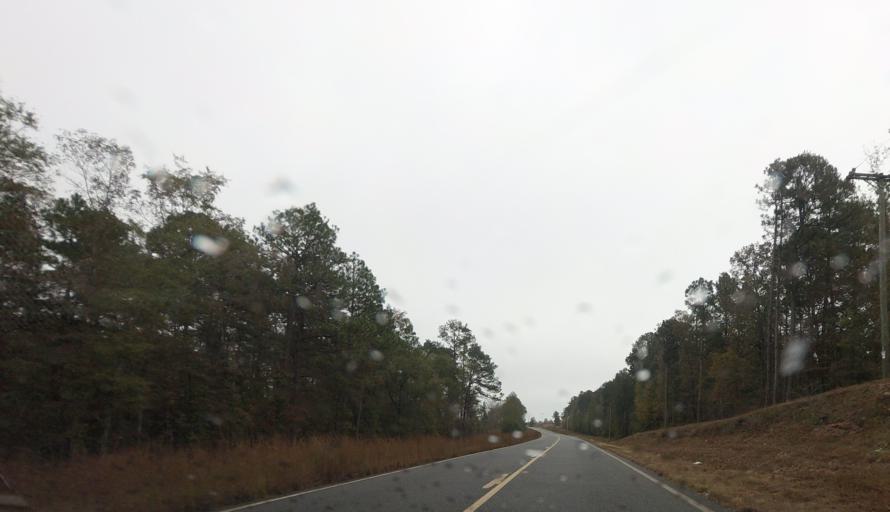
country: US
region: Georgia
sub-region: Taylor County
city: Butler
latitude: 32.4360
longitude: -84.3515
